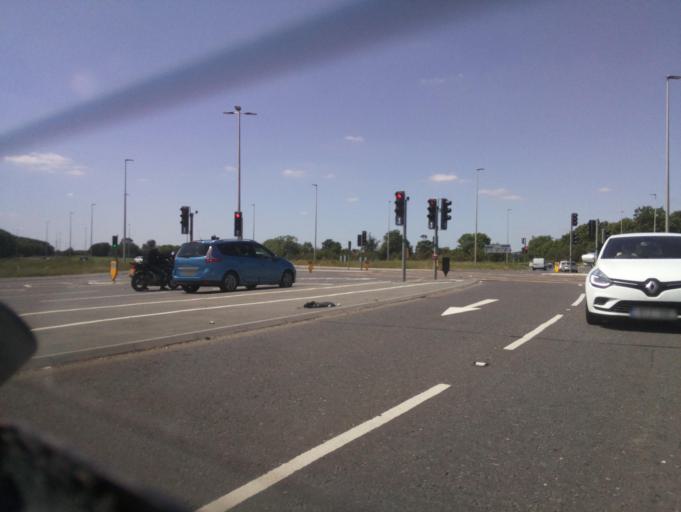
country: GB
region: England
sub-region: Wiltshire
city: Lydiard Tregoze
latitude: 51.5438
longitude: -1.8545
